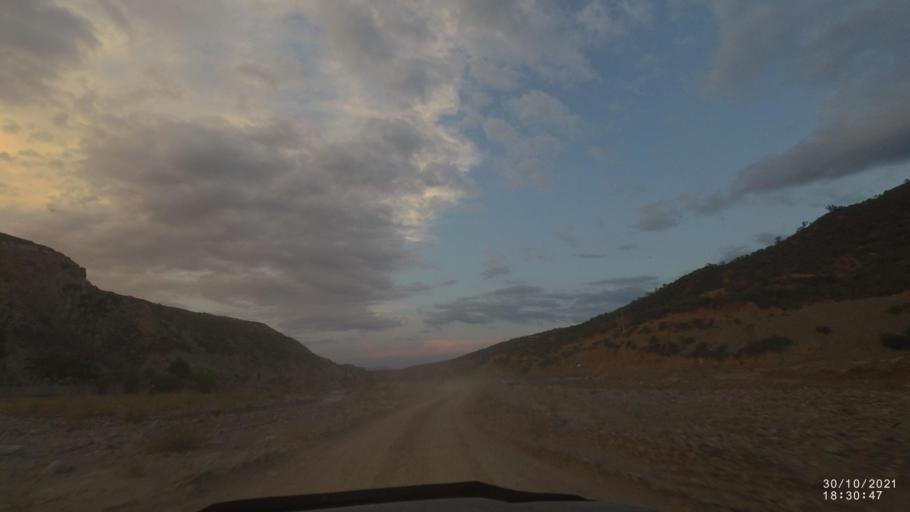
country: BO
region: Cochabamba
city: Sipe Sipe
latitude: -17.5610
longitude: -66.3812
